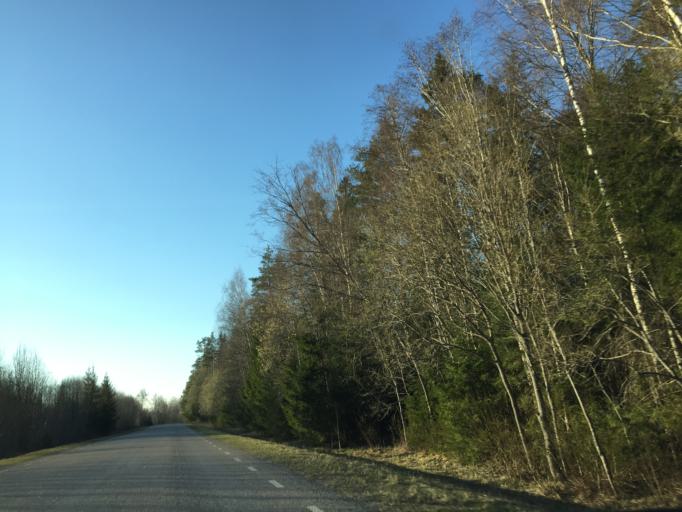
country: EE
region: Ida-Virumaa
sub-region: Toila vald
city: Voka
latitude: 59.1751
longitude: 27.5699
